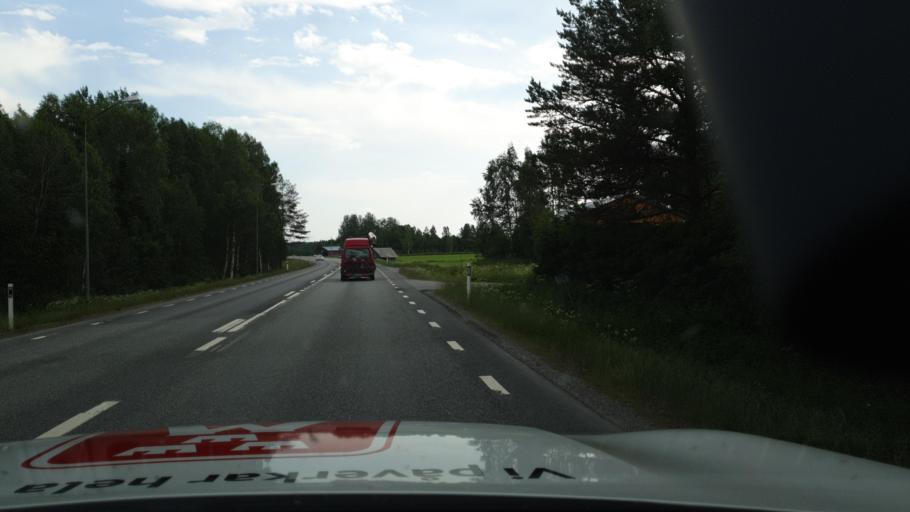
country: SE
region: Vaesterbotten
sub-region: Skelleftea Kommun
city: Burea
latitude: 64.5121
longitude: 21.2572
